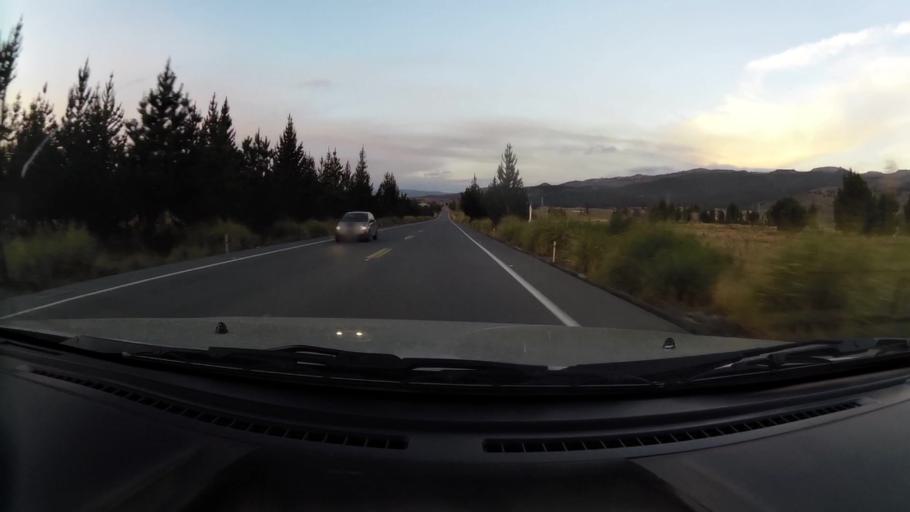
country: EC
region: Chimborazo
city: Alausi
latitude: -2.0259
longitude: -78.7339
